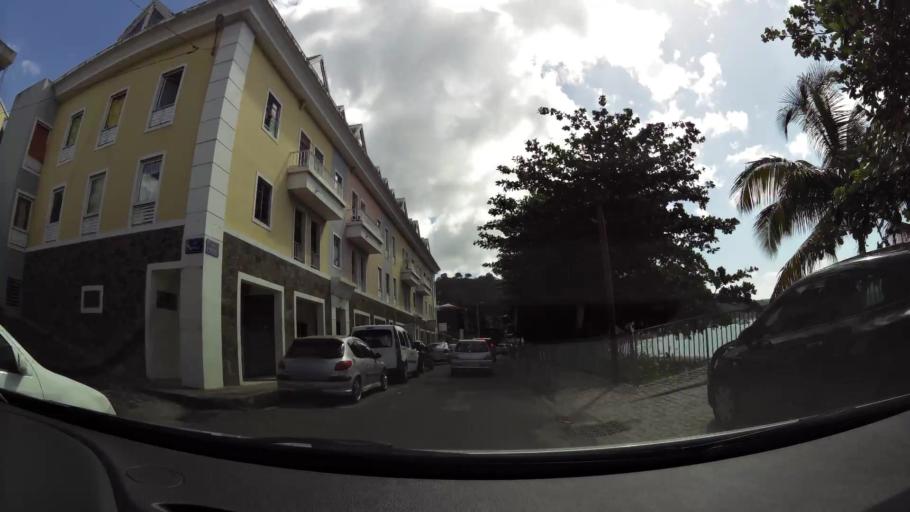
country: MQ
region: Martinique
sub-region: Martinique
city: Saint-Pierre
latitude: 14.7465
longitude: -61.1771
